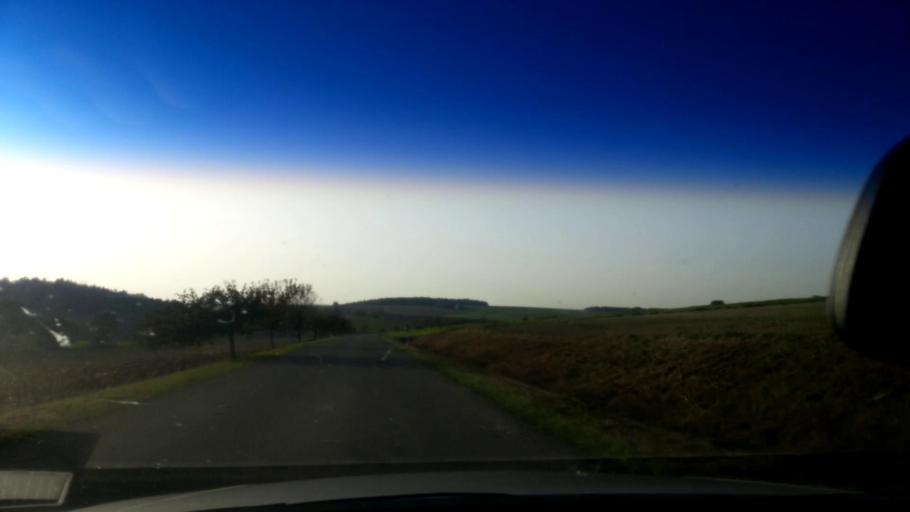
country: DE
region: Bavaria
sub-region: Upper Franconia
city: Ebensfeld
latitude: 50.0275
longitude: 10.9832
